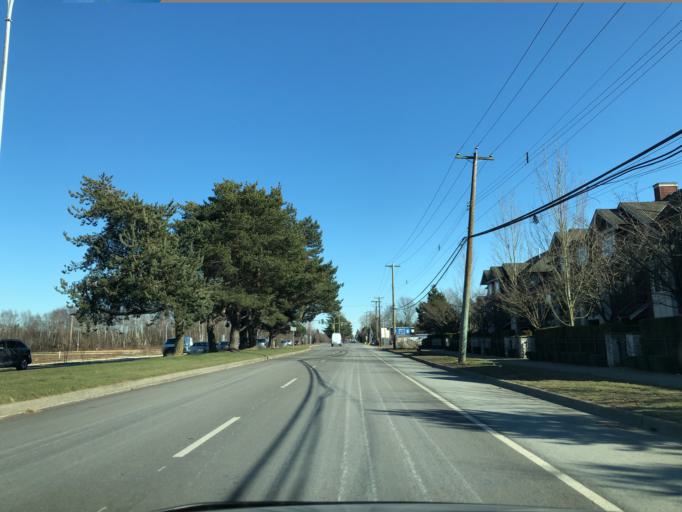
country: CA
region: British Columbia
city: Richmond
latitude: 49.1700
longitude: -123.1170
